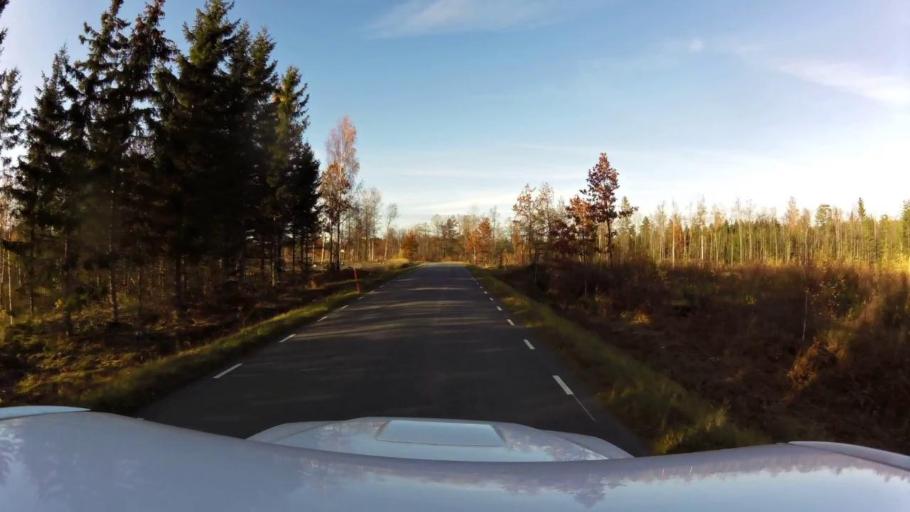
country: SE
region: OEstergoetland
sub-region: Linkopings Kommun
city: Sturefors
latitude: 58.2724
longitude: 15.6642
